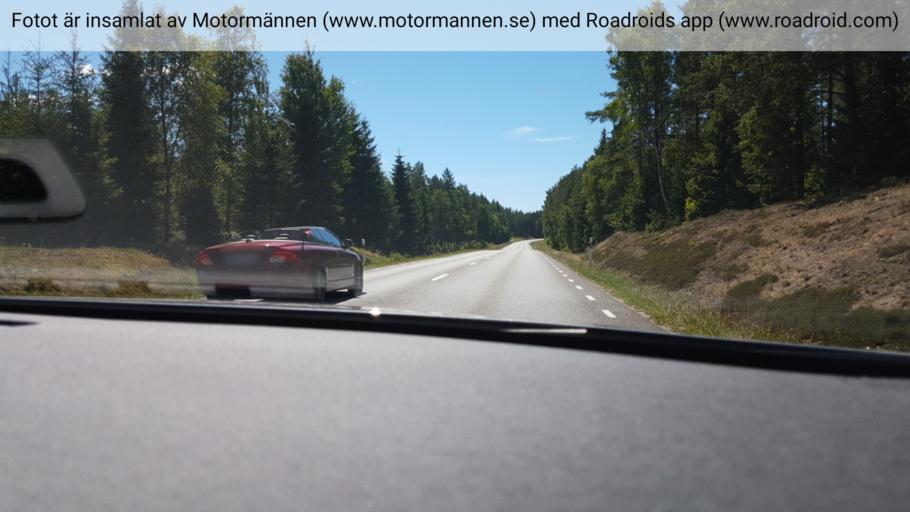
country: SE
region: Joenkoeping
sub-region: Gnosjo Kommun
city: Marieholm
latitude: 57.6422
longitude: 13.8023
